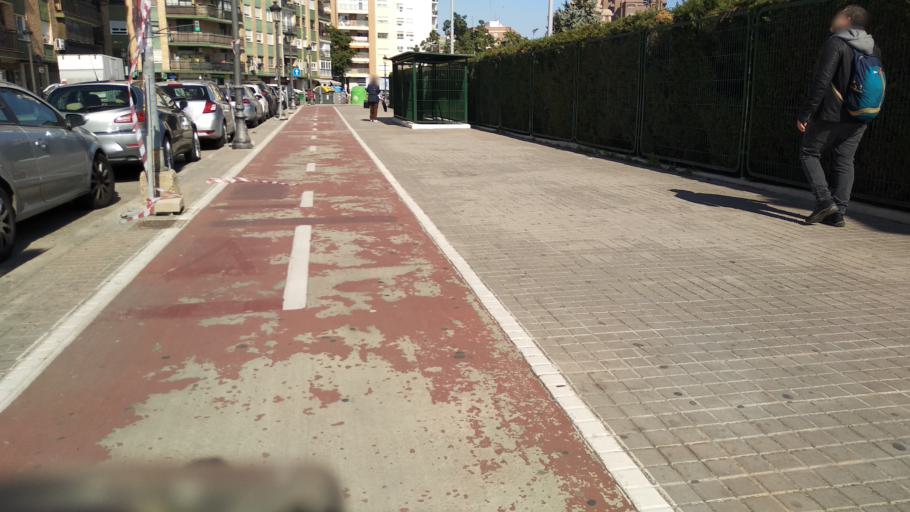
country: ES
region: Valencia
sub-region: Provincia de Valencia
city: Valencia
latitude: 39.4799
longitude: -0.3610
